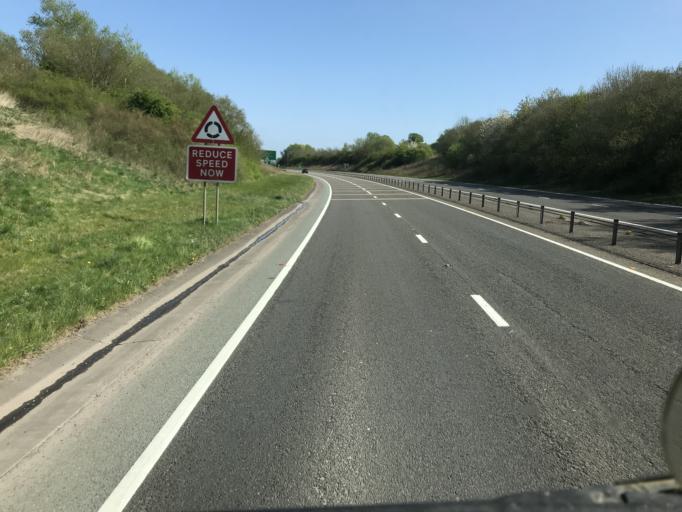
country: GB
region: England
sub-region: Cheshire East
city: Weston
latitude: 53.0693
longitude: -2.3904
